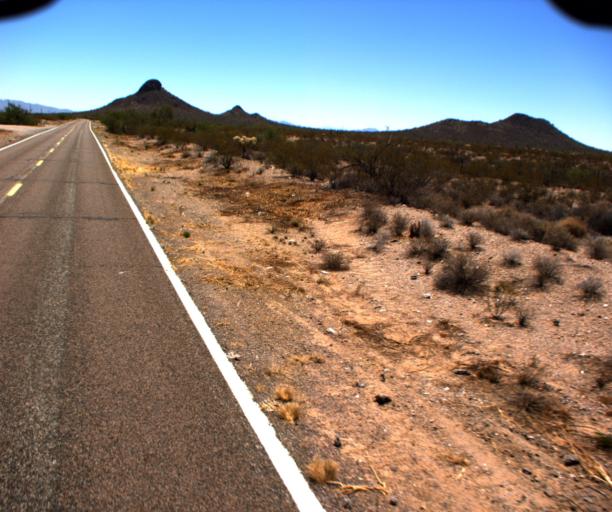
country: US
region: Arizona
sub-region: Pima County
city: Ajo
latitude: 32.2047
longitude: -112.5504
